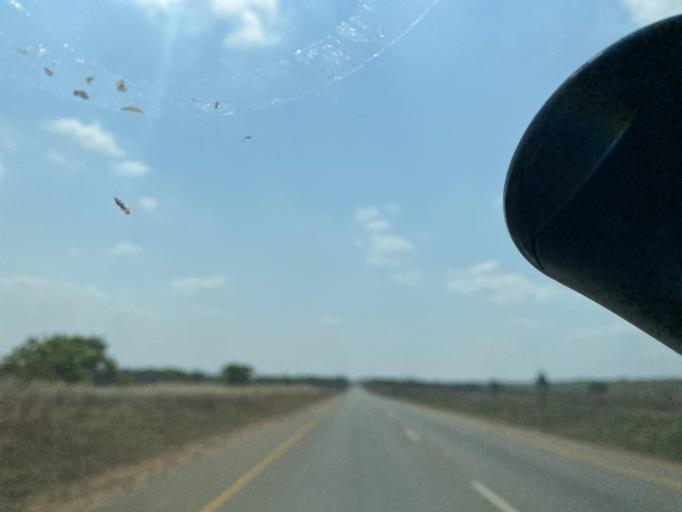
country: ZM
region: Lusaka
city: Chongwe
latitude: -15.5422
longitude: 28.6617
